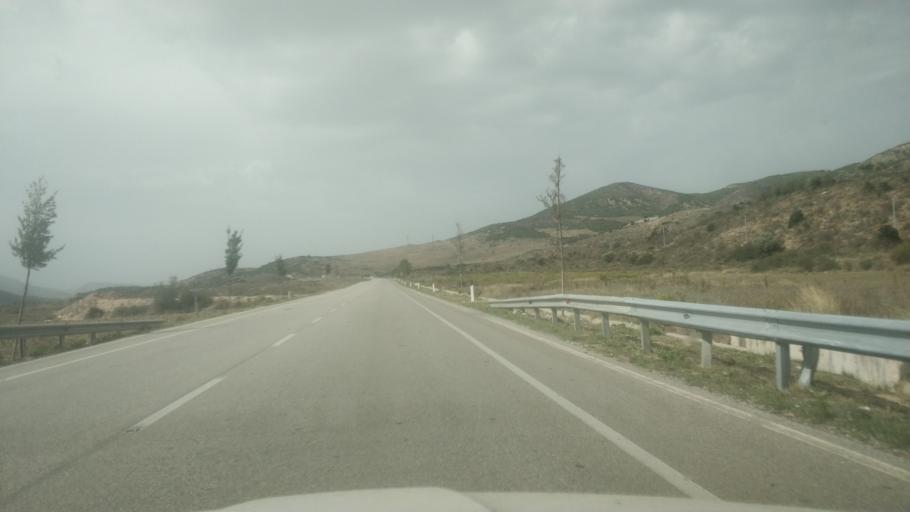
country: AL
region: Gjirokaster
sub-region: Rrethi i Tepelenes
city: Memaliaj
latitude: 40.3588
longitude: 19.9318
